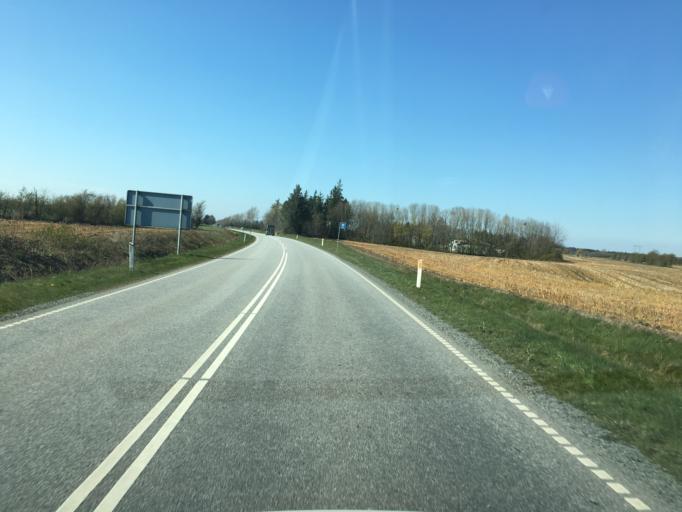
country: DK
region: South Denmark
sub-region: Aabenraa Kommune
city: Krusa
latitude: 54.9415
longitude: 9.3606
